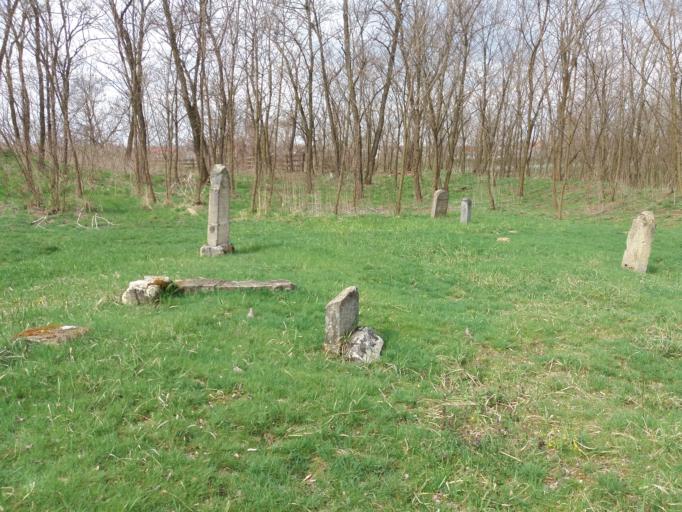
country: HU
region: Szabolcs-Szatmar-Bereg
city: Petnehaza
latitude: 48.0520
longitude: 22.0456
